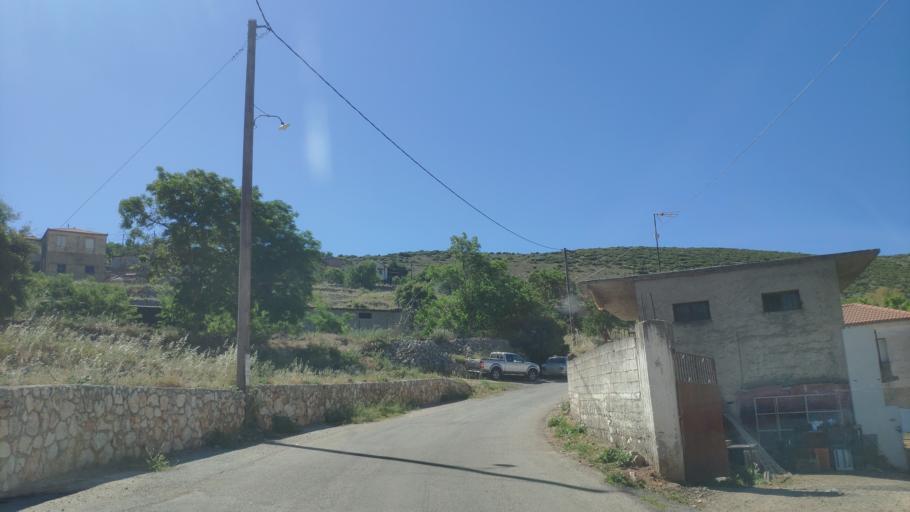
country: GR
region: Peloponnese
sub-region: Nomos Korinthias
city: Khiliomodhi
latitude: 37.7536
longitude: 22.8777
